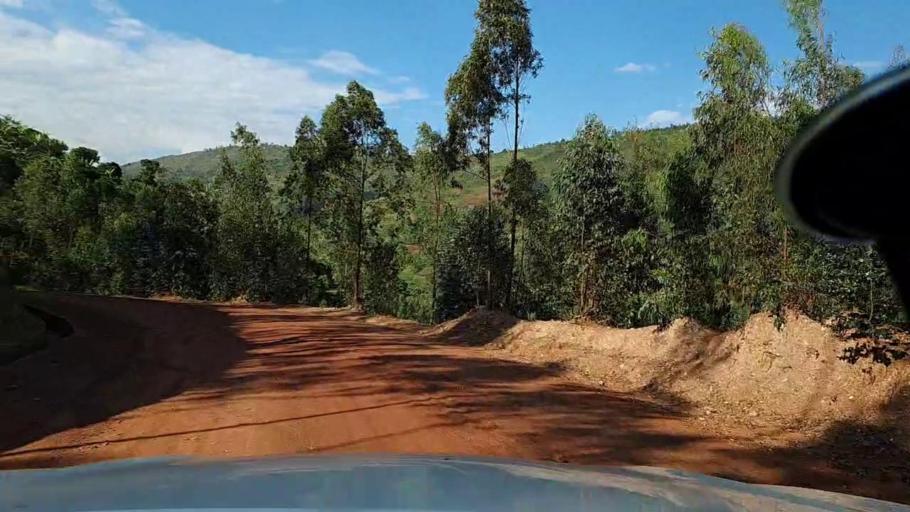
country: RW
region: Kigali
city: Kigali
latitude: -1.8459
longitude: 29.8656
